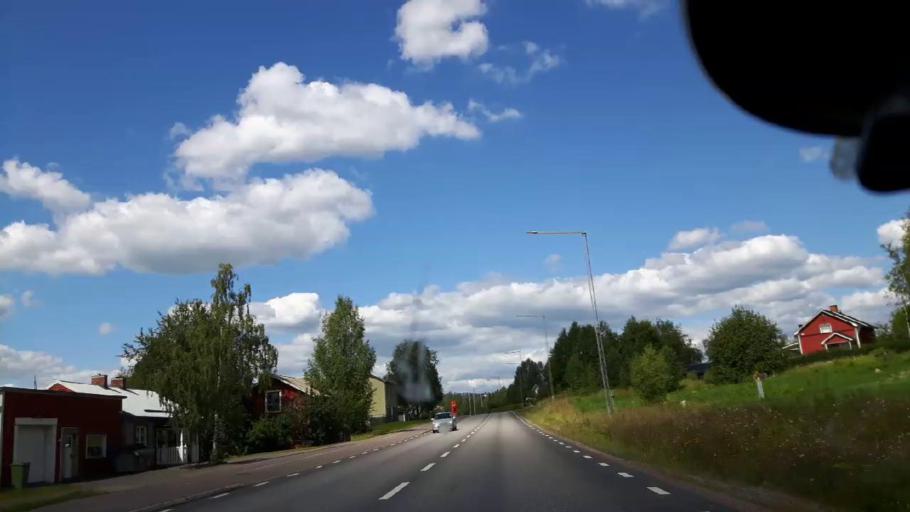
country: SE
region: Jaemtland
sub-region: Ragunda Kommun
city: Hammarstrand
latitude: 63.0075
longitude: 16.6652
